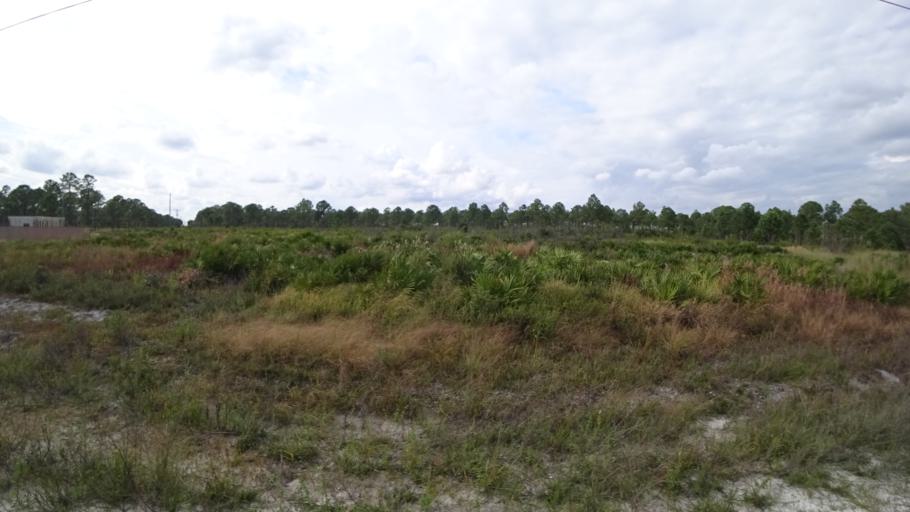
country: US
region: Florida
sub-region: Hillsborough County
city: Wimauma
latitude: 27.5458
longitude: -82.1267
